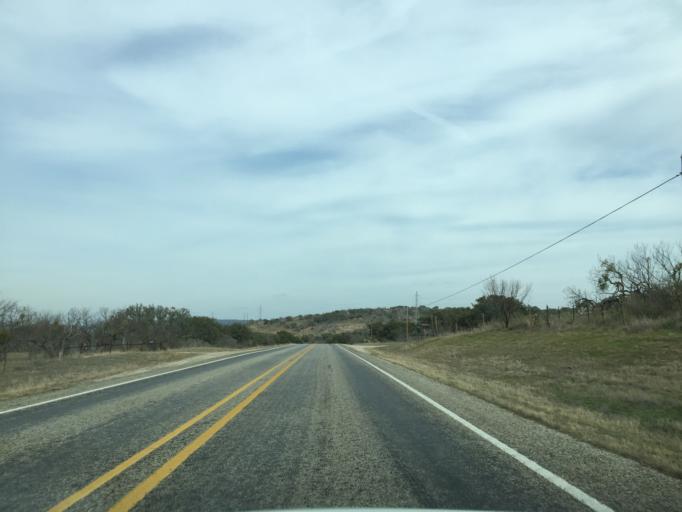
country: US
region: Texas
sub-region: Gillespie County
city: Fredericksburg
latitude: 30.4666
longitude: -98.7195
